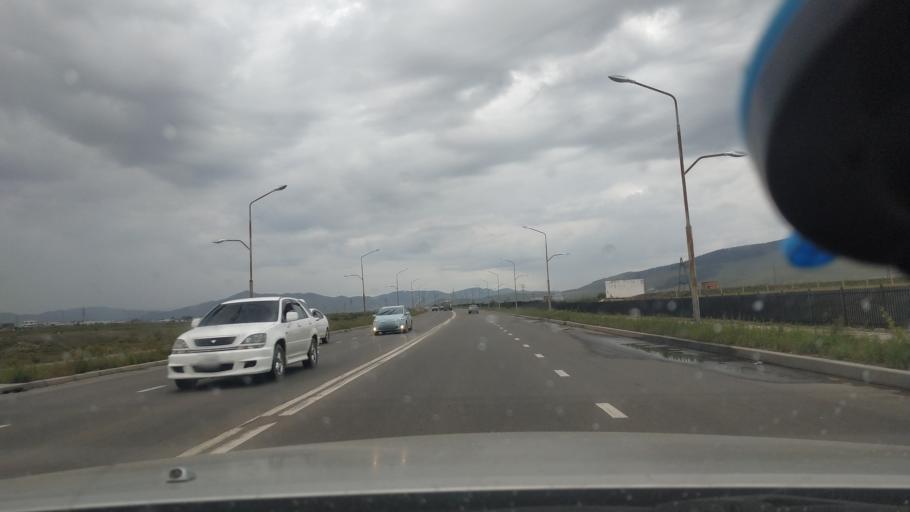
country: MN
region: Ulaanbaatar
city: Ulaanbaatar
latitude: 47.9017
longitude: 106.9855
